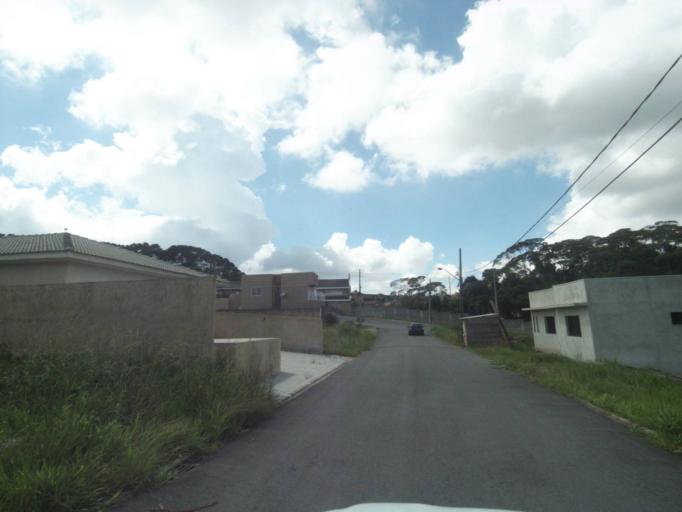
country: BR
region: Parana
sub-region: Colombo
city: Colombo
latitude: -25.3135
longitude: -49.2327
